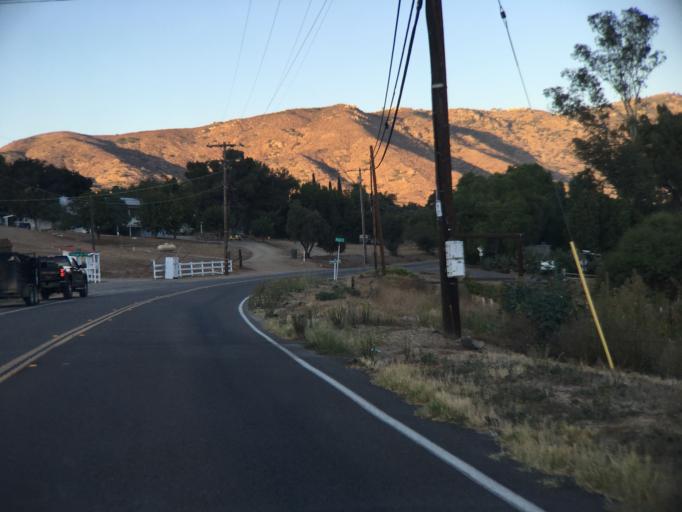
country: US
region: California
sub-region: San Diego County
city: Harbison Canyon
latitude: 32.7962
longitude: -116.8294
